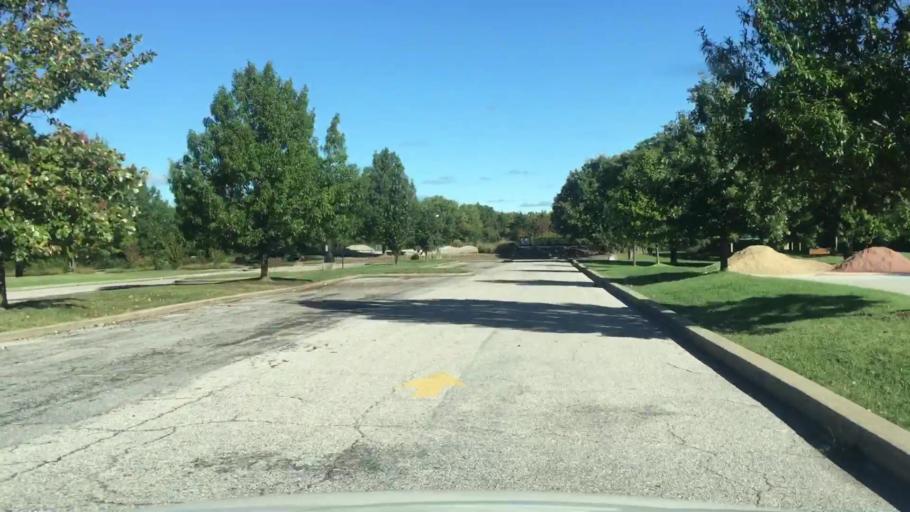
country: US
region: Missouri
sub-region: Boone County
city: Columbia
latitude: 38.9771
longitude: -92.3634
